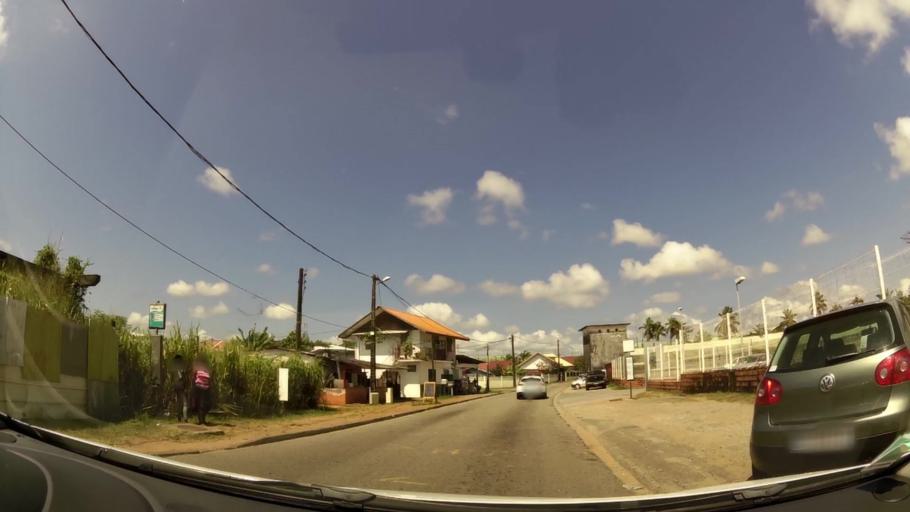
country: GF
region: Guyane
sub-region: Guyane
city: Cayenne
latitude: 4.9223
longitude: -52.3214
